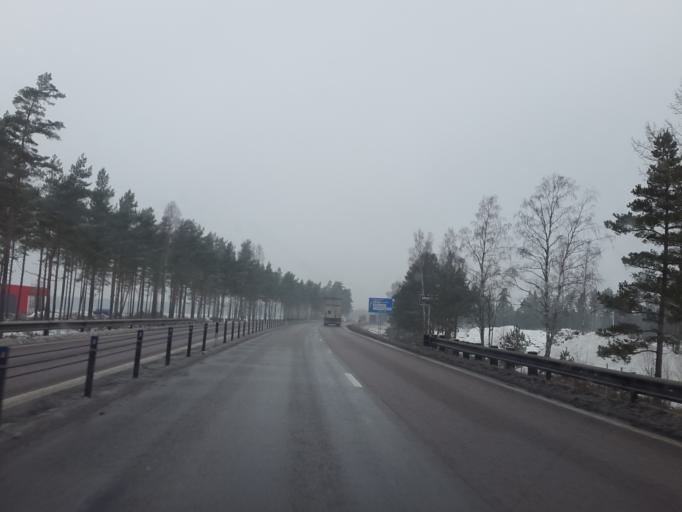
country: SE
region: Joenkoeping
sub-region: Jonkopings Kommun
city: Jonkoping
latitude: 57.7678
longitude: 14.0907
